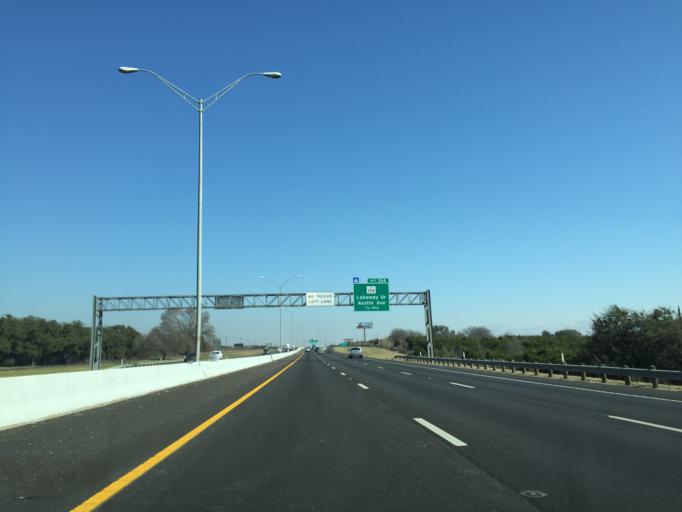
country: US
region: Texas
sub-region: Williamson County
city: Georgetown
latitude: 30.6582
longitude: -97.6741
